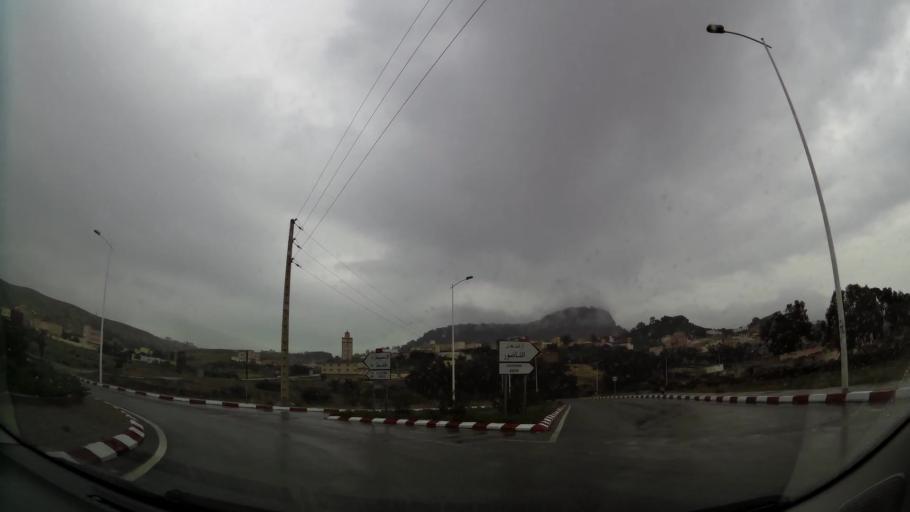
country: MA
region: Oriental
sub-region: Nador
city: Nador
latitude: 35.1435
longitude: -3.0141
